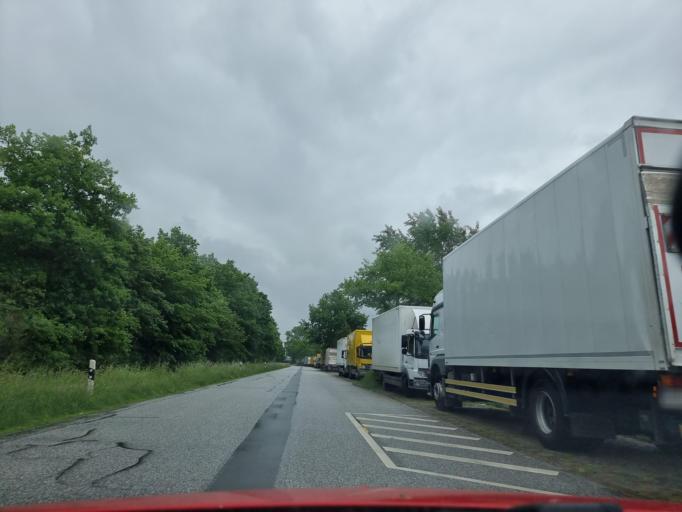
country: DE
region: Hamburg
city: Harburg
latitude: 53.4970
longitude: 9.9666
